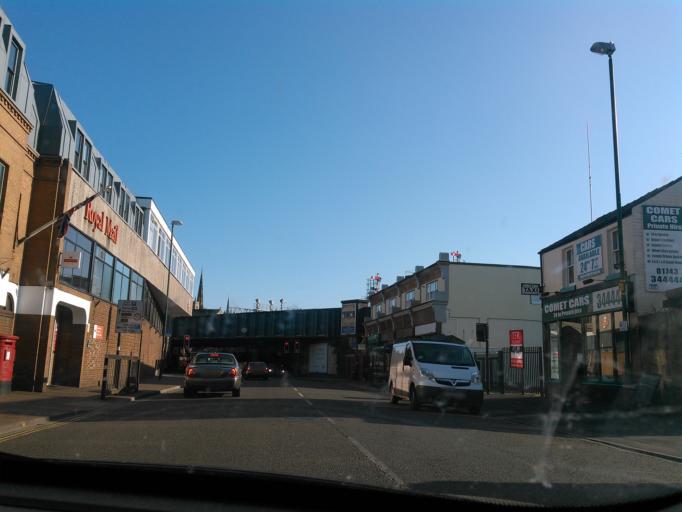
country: GB
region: England
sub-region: Shropshire
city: Shrewsbury
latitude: 52.7135
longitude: -2.7497
